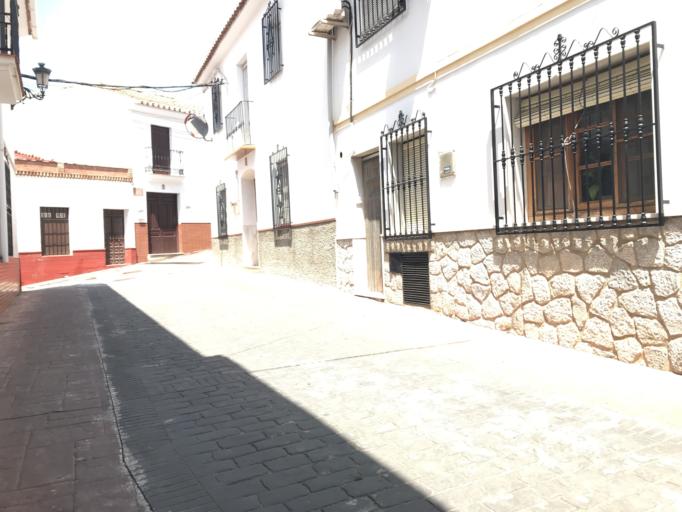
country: ES
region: Andalusia
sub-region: Provincia de Malaga
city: Periana
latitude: 36.9279
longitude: -4.1920
